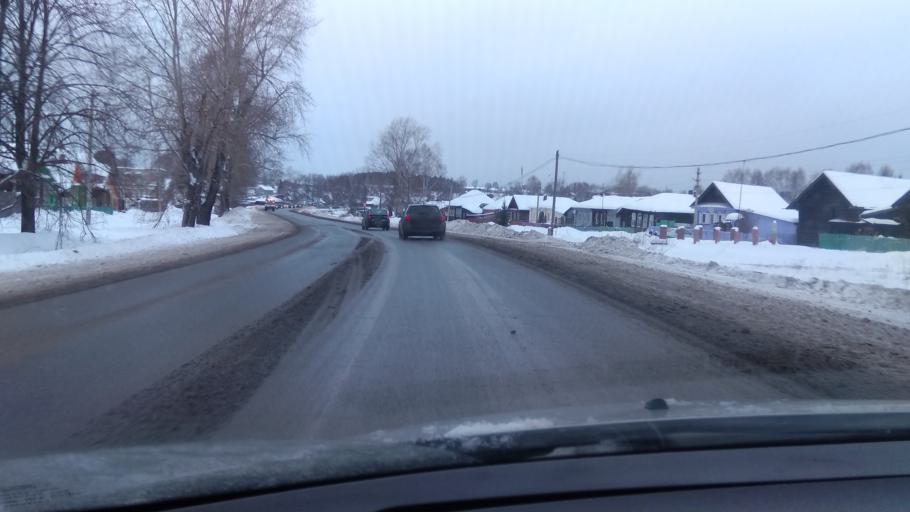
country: RU
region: Sverdlovsk
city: Nikolo-Pavlovskoye
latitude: 57.7832
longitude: 60.0593
